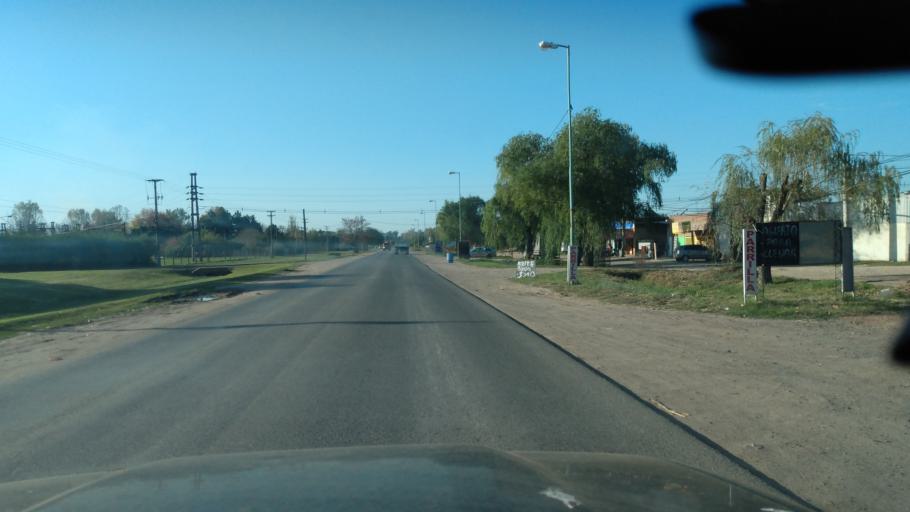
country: AR
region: Buenos Aires
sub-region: Partido de Lujan
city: Lujan
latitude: -34.5439
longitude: -59.1222
